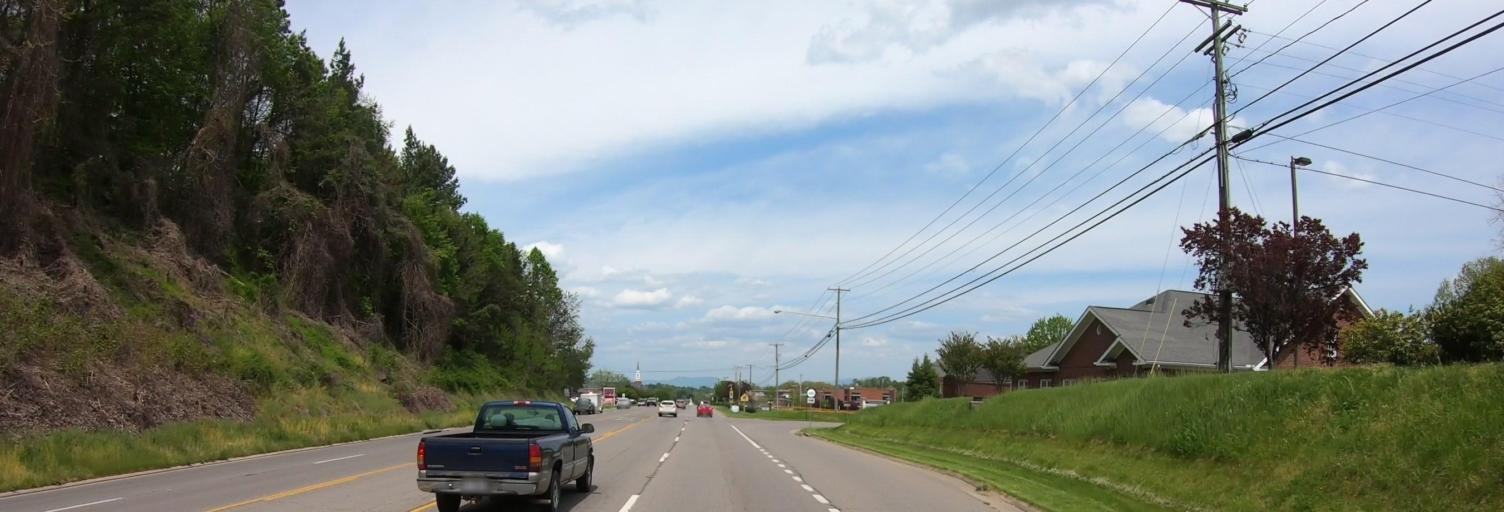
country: US
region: Virginia
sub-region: Roanoke County
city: Cave Spring
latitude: 37.2123
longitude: -80.0206
